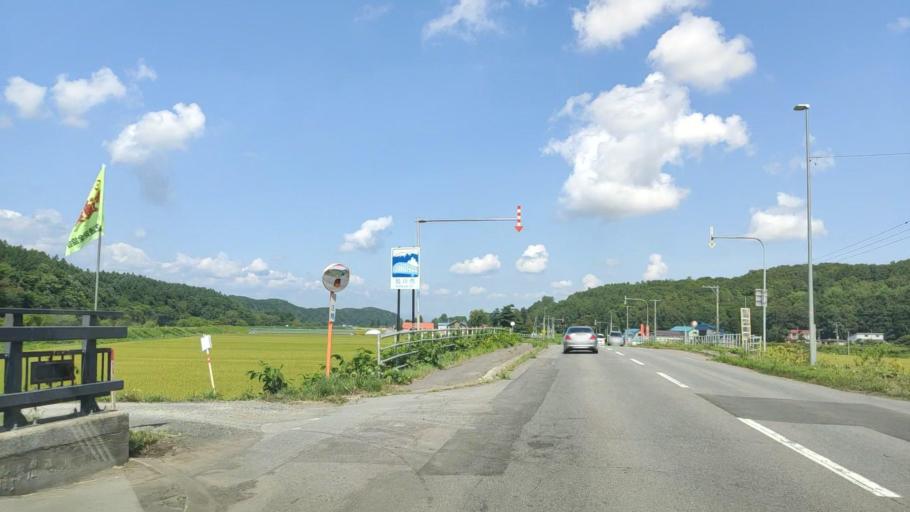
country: JP
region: Hokkaido
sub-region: Asahikawa-shi
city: Asahikawa
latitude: 43.6253
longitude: 142.4665
